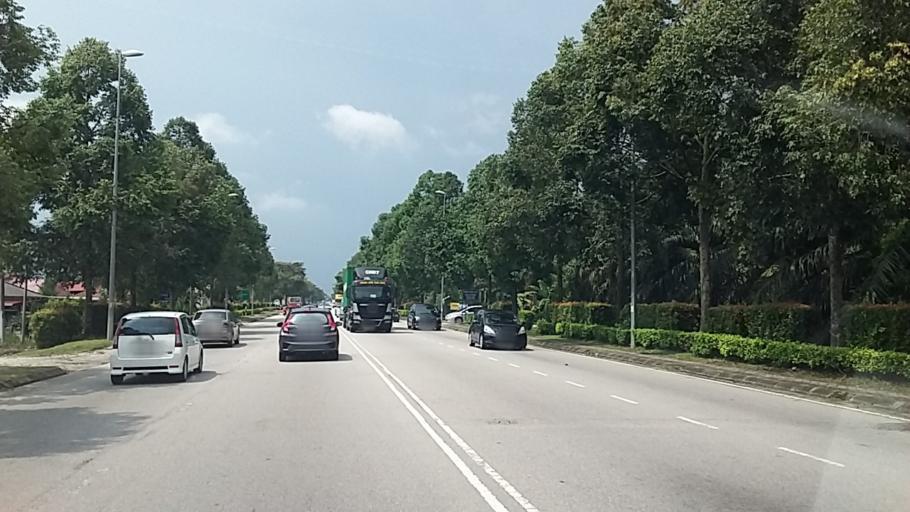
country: MY
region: Johor
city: Parit Raja
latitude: 1.8590
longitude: 103.1019
